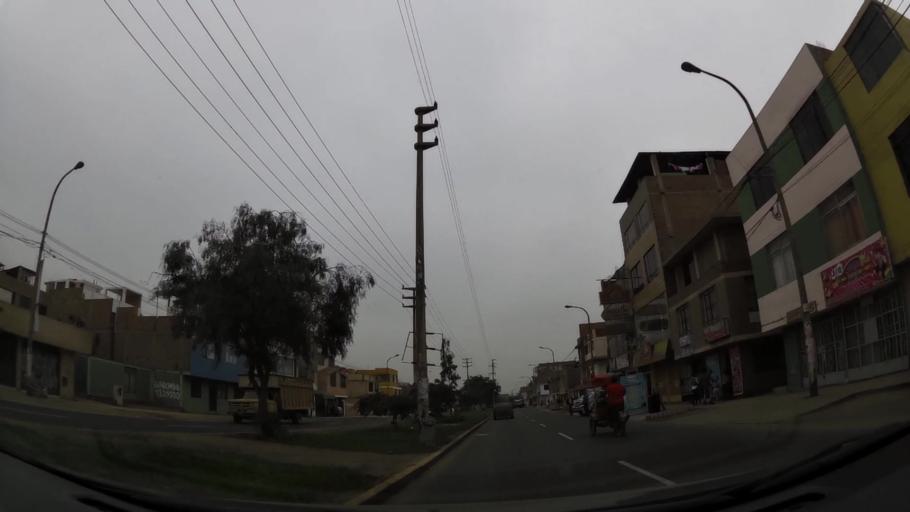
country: PE
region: Lima
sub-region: Lima
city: Urb. Santo Domingo
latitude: -11.8887
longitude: -77.0366
